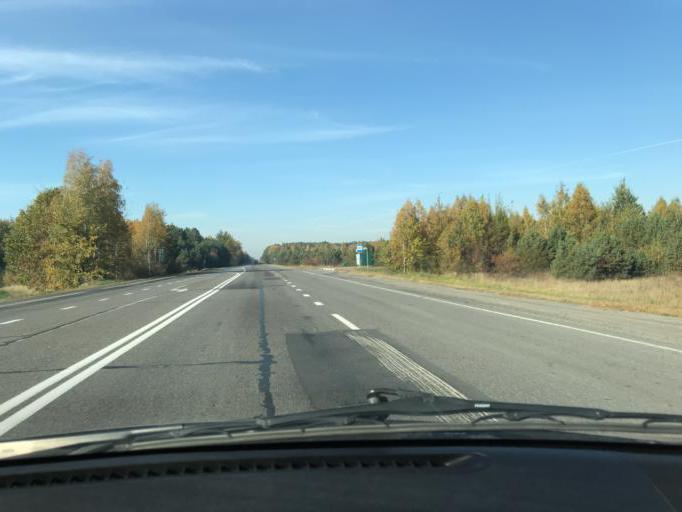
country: BY
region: Brest
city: Davyd-Haradok
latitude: 52.2449
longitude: 27.1396
